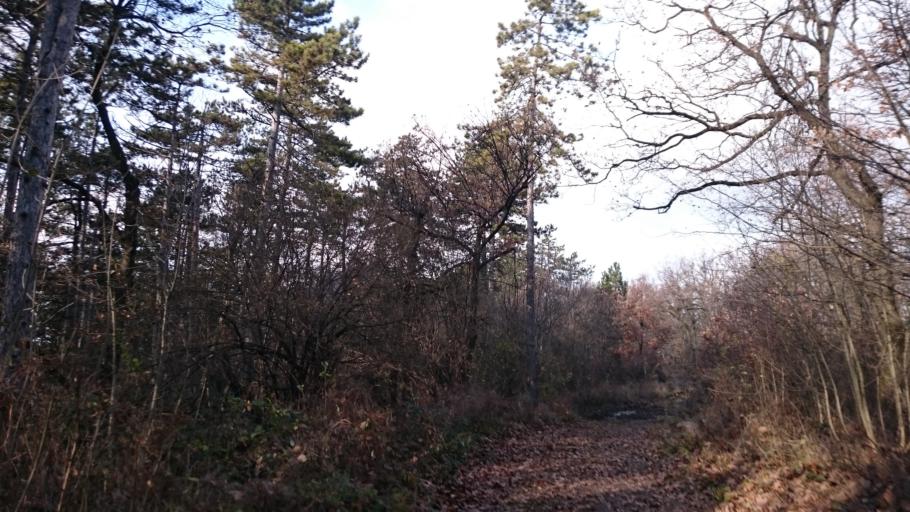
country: HU
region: Pest
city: Pilisborosjeno
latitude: 47.6166
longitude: 18.9962
